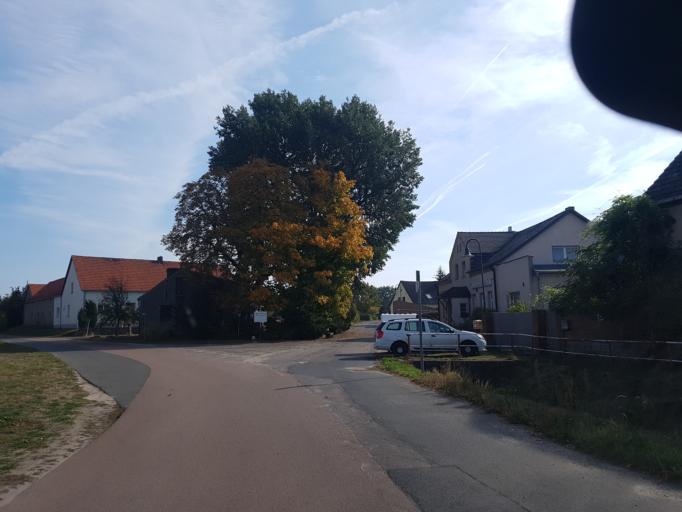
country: DE
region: Brandenburg
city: Ihlow
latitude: 51.8823
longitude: 13.2455
